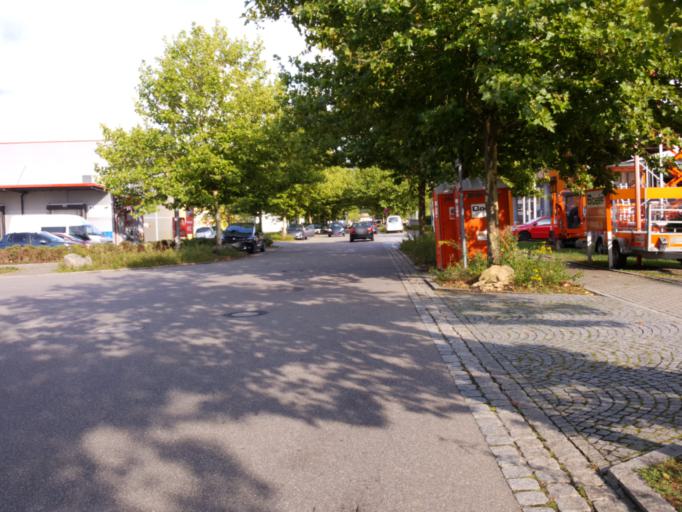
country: DE
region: Baden-Wuerttemberg
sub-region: Freiburg Region
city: Eimeldingen
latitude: 47.6245
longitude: 7.6060
